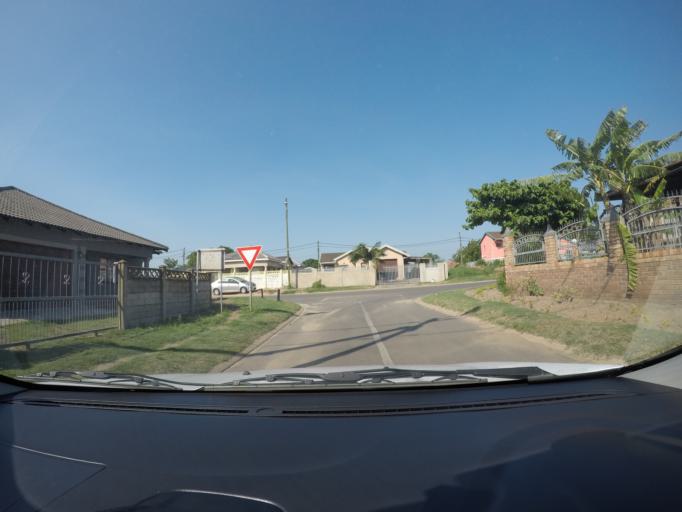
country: ZA
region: KwaZulu-Natal
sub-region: uThungulu District Municipality
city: Richards Bay
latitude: -28.7204
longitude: 32.0375
